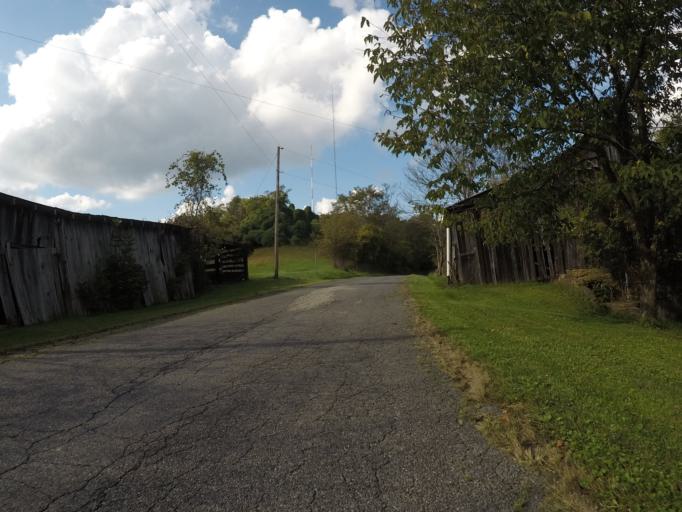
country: US
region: West Virginia
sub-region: Wayne County
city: Lavalette
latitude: 38.3649
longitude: -82.4735
